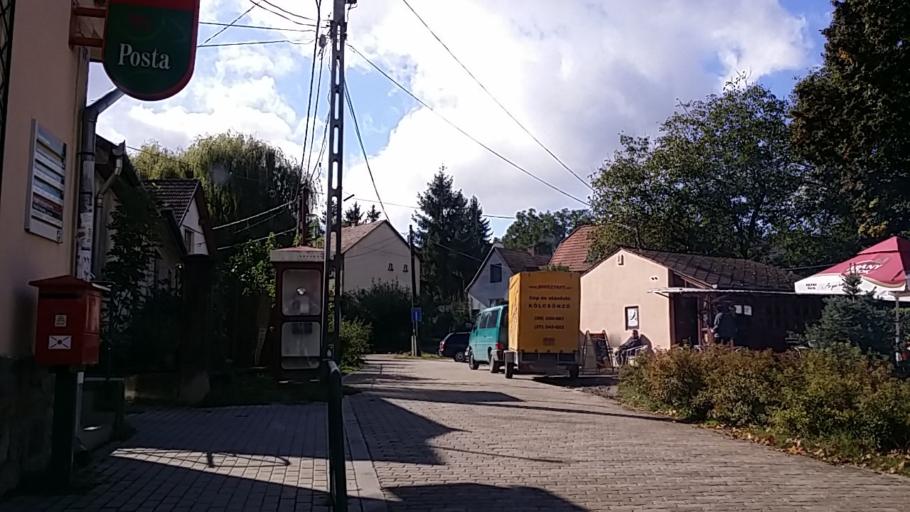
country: HU
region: Pest
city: Csobanka
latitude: 47.6417
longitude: 18.9681
